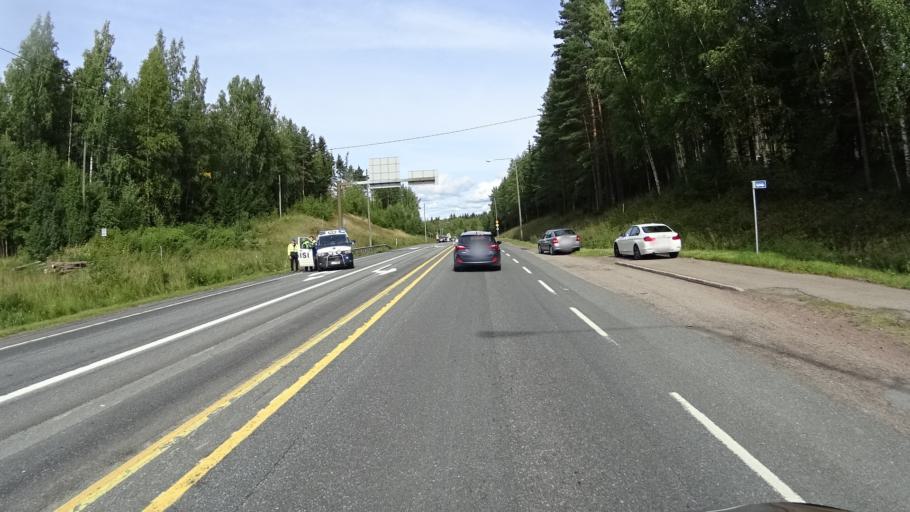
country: FI
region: Pirkanmaa
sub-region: Tampere
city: Haemeenkyroe
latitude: 61.6762
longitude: 23.1605
